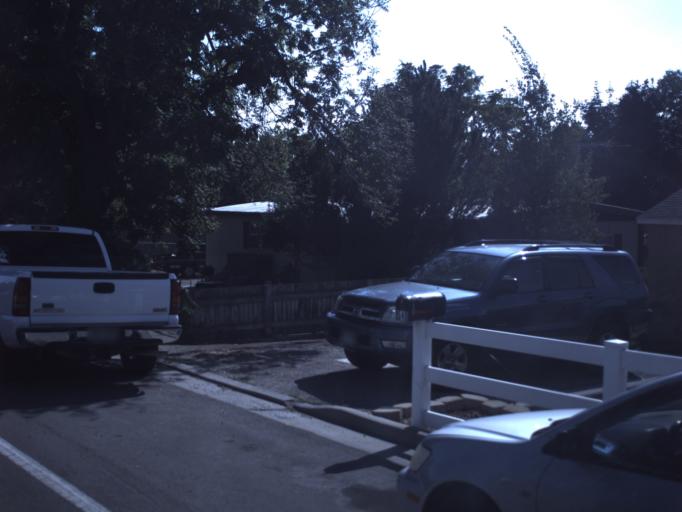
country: US
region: Utah
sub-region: Utah County
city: Pleasant Grove
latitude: 40.3574
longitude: -111.7408
